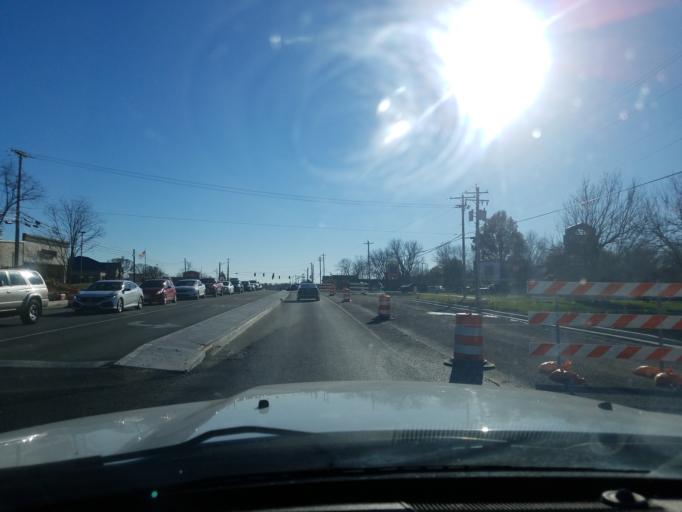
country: US
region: Indiana
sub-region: Clark County
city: Oak Park
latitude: 38.3279
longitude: -85.7118
